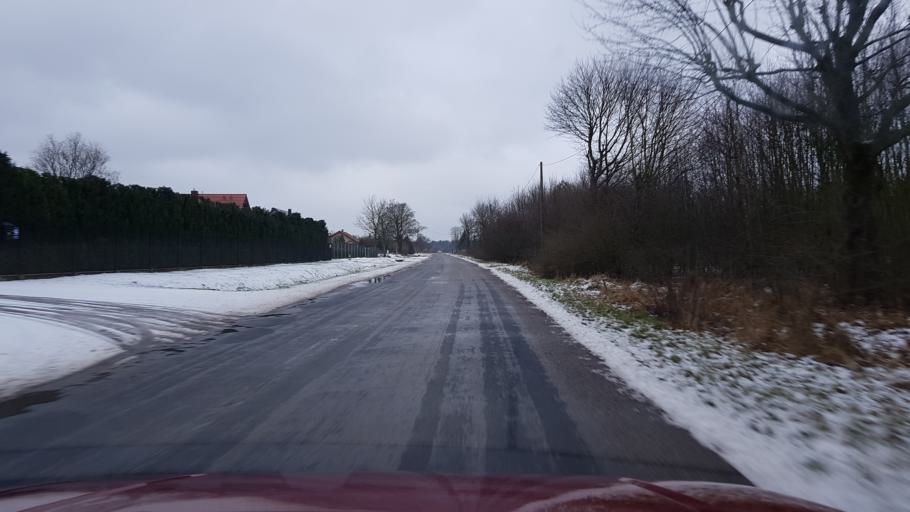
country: PL
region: West Pomeranian Voivodeship
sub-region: Powiat goleniowski
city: Nowogard
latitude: 53.6504
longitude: 15.1234
